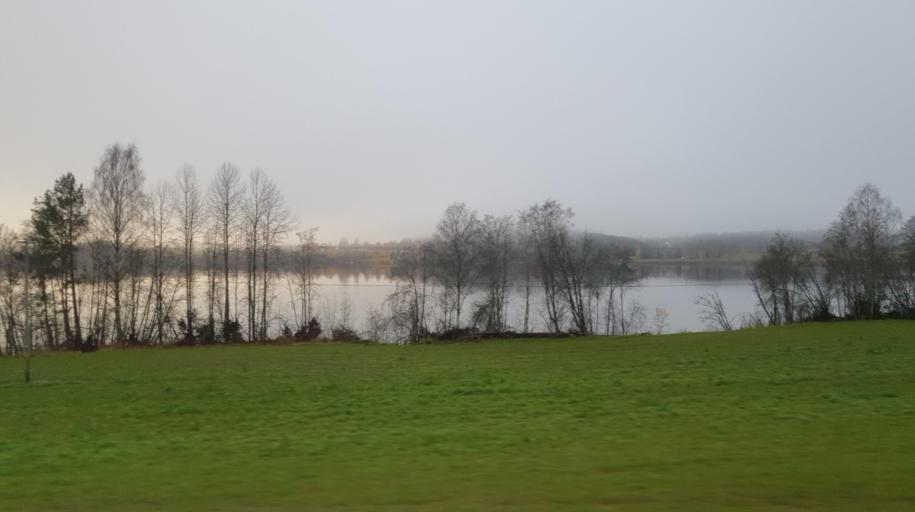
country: NO
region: Buskerud
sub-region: Krodsherad
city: Noresund
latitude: 60.1484
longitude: 9.7619
